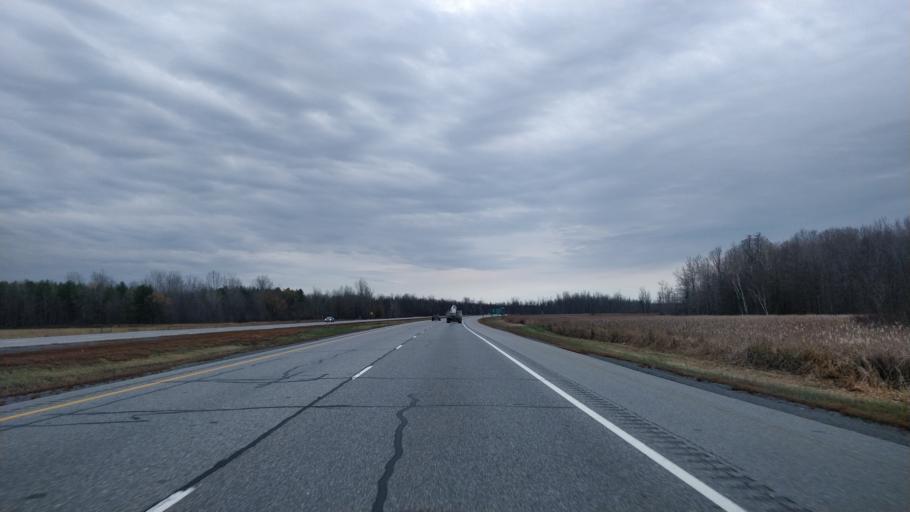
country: CA
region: Ontario
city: Bells Corners
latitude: 45.1071
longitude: -75.6639
